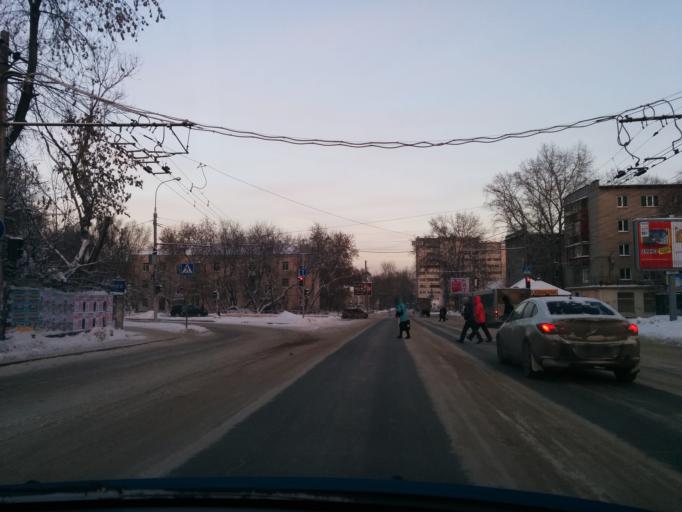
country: RU
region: Perm
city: Perm
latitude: 57.9985
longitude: 56.2705
